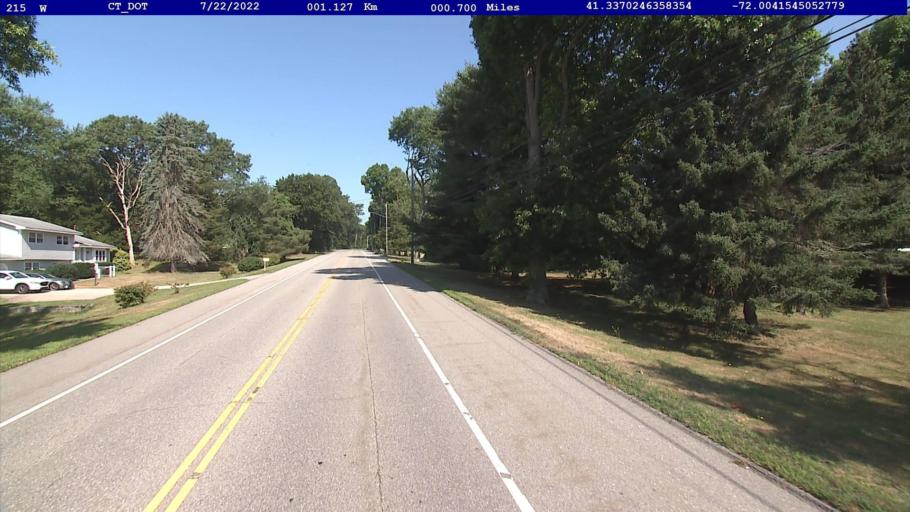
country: US
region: Connecticut
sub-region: New London County
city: Noank
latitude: 41.3370
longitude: -72.0042
